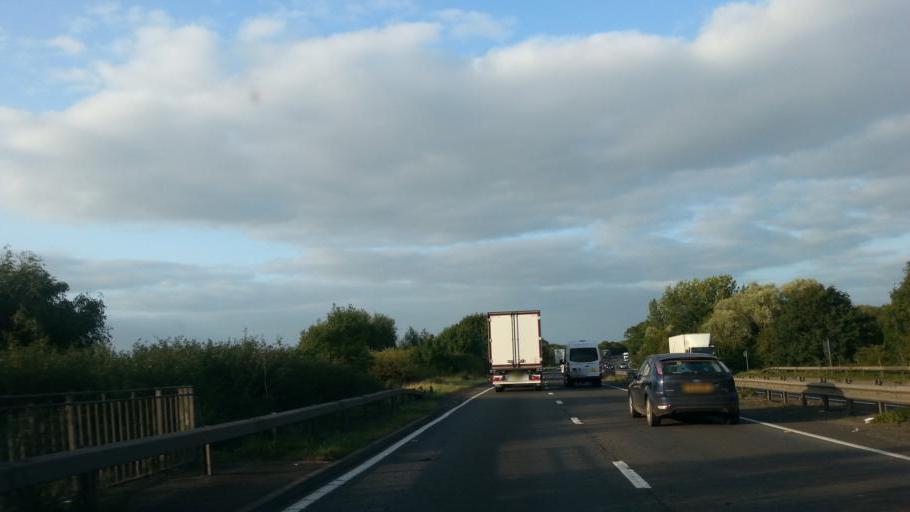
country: GB
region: England
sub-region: Oxfordshire
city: Yarnton
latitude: 51.7814
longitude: -1.3029
